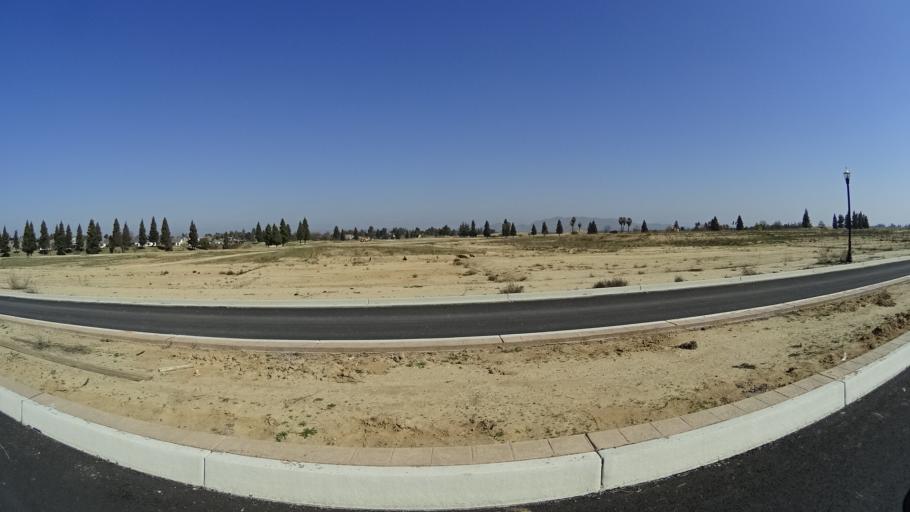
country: US
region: California
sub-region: Fresno County
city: Clovis
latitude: 36.9051
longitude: -119.7404
